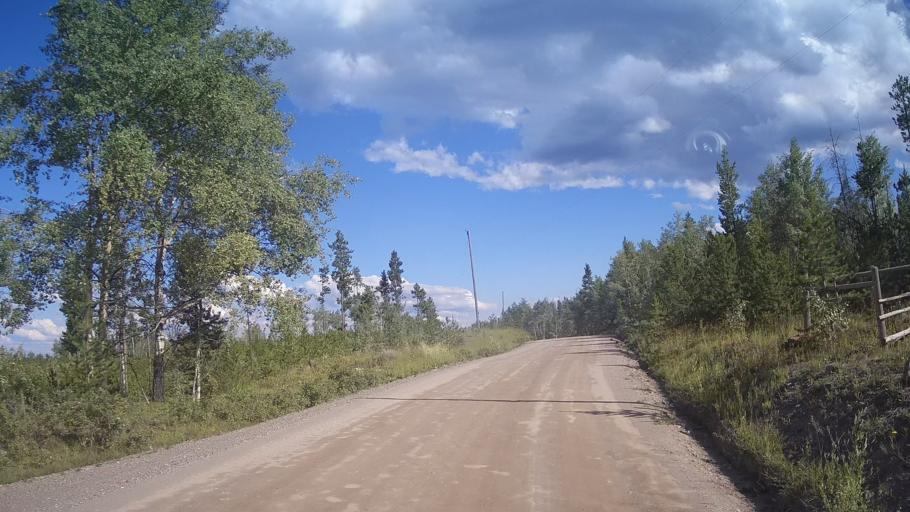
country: CA
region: British Columbia
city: Cache Creek
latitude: 51.2570
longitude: -121.6806
